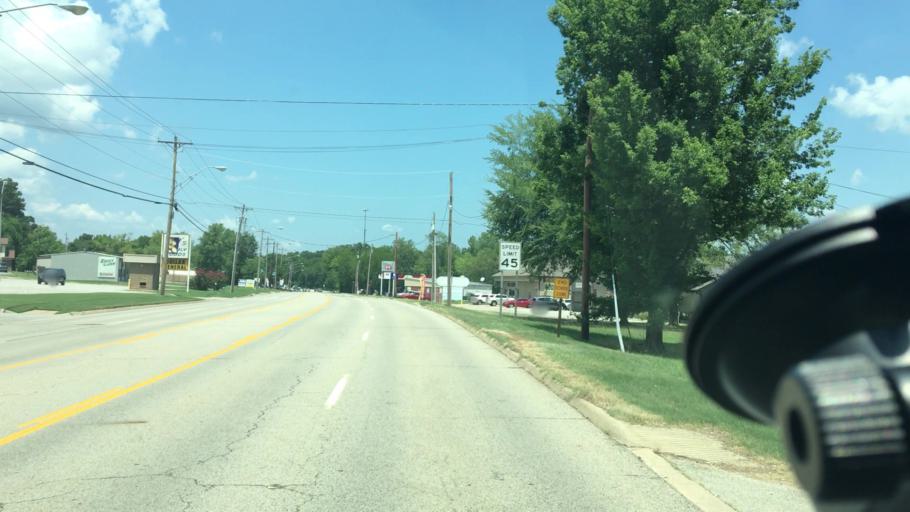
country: US
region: Arkansas
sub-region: Sebastian County
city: Barling
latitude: 35.3312
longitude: -94.3083
